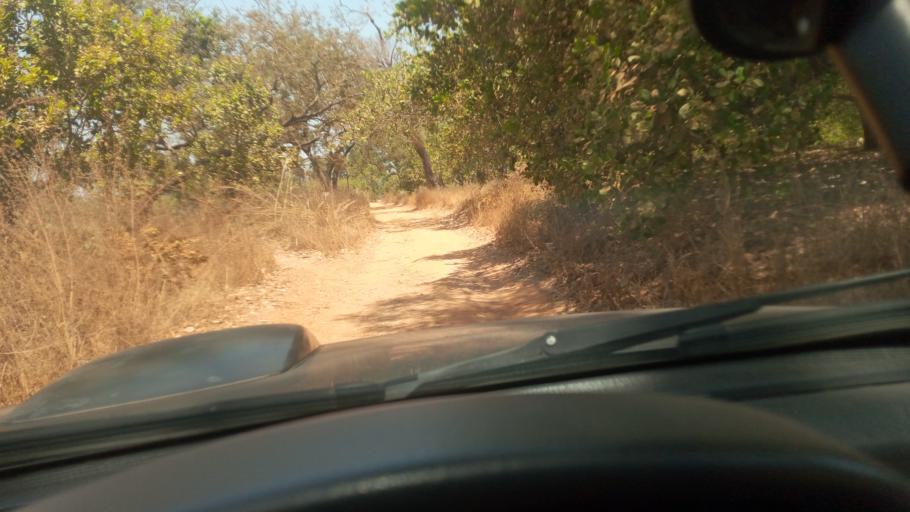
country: GW
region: Oio
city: Farim
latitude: 12.4558
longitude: -15.3071
